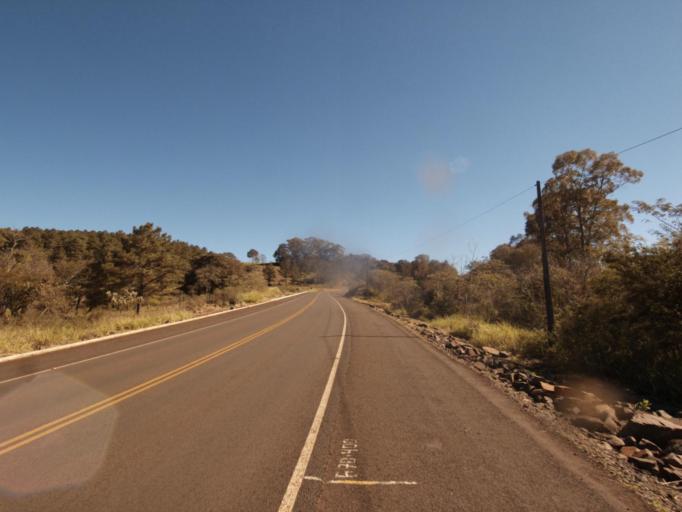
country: AR
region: Misiones
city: Bernardo de Irigoyen
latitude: -26.6177
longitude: -53.6570
